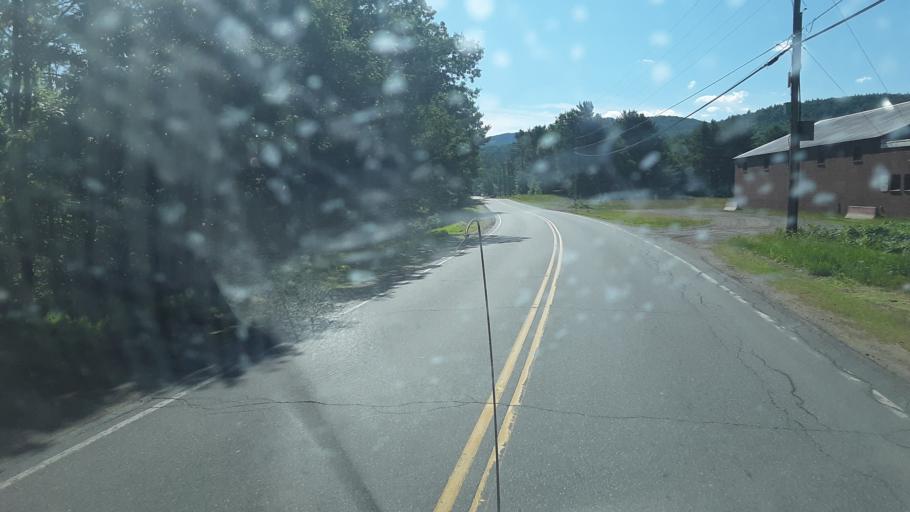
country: US
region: New Hampshire
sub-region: Grafton County
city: North Haverhill
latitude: 44.0786
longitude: -71.9920
